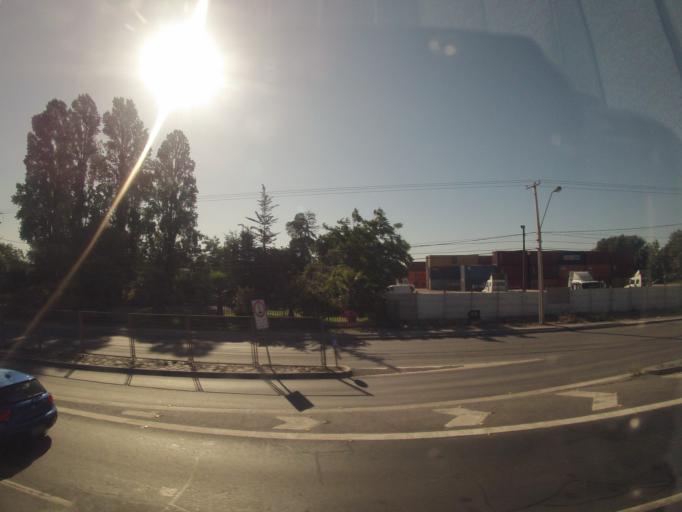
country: CL
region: Santiago Metropolitan
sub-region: Provincia de Maipo
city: Buin
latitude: -33.6712
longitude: -70.7221
